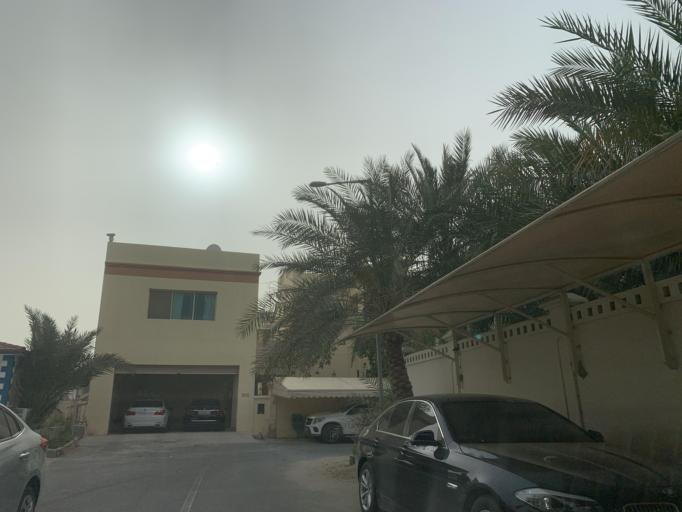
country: BH
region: Central Governorate
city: Madinat Hamad
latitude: 26.1384
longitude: 50.5255
